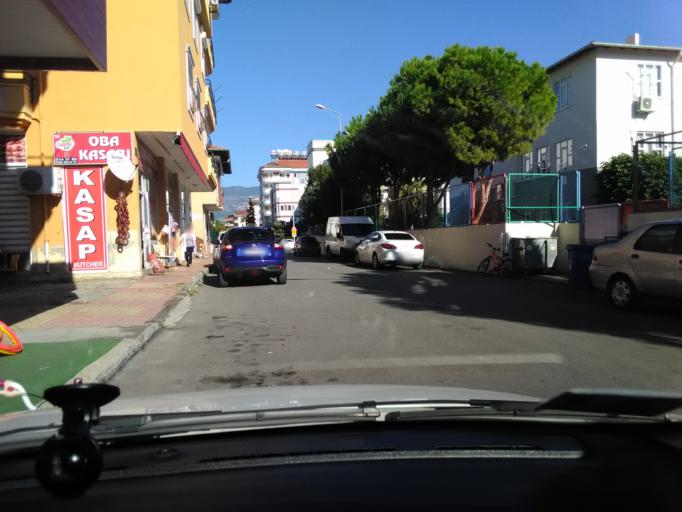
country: TR
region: Antalya
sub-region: Alanya
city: Alanya
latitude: 36.5356
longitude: 32.0412
